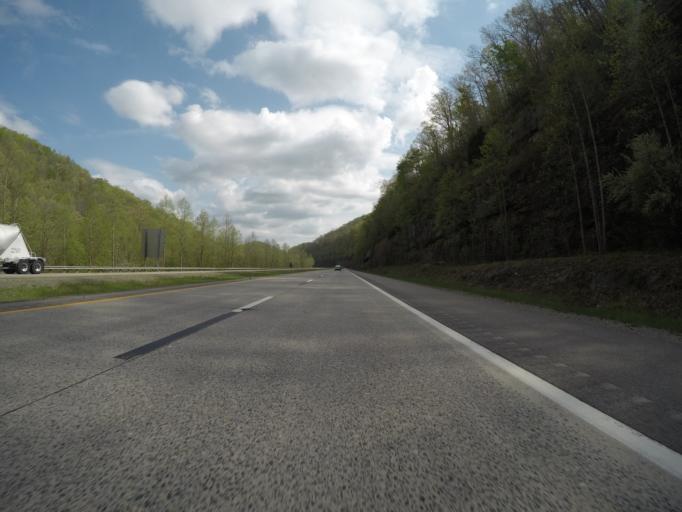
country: US
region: West Virginia
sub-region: Kanawha County
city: Alum Creek
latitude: 38.1882
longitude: -81.8486
